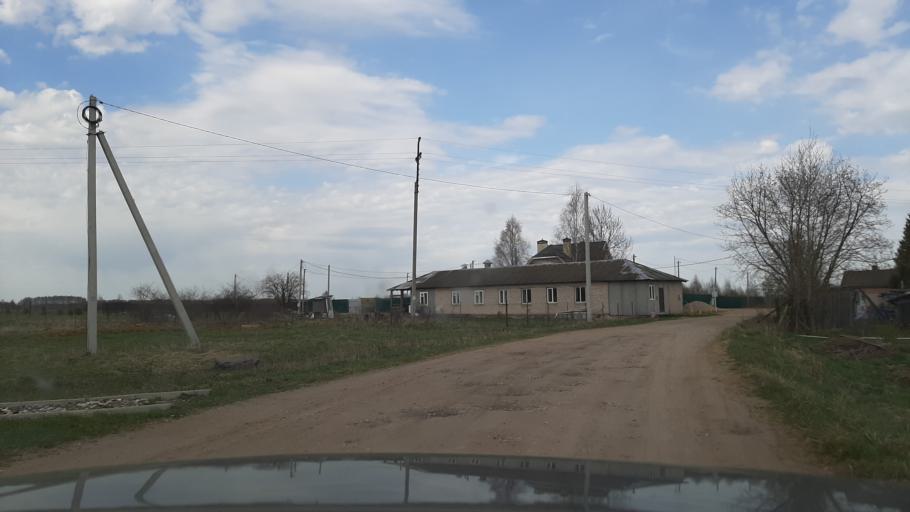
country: RU
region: Ivanovo
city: Furmanov
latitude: 57.3194
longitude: 41.1567
